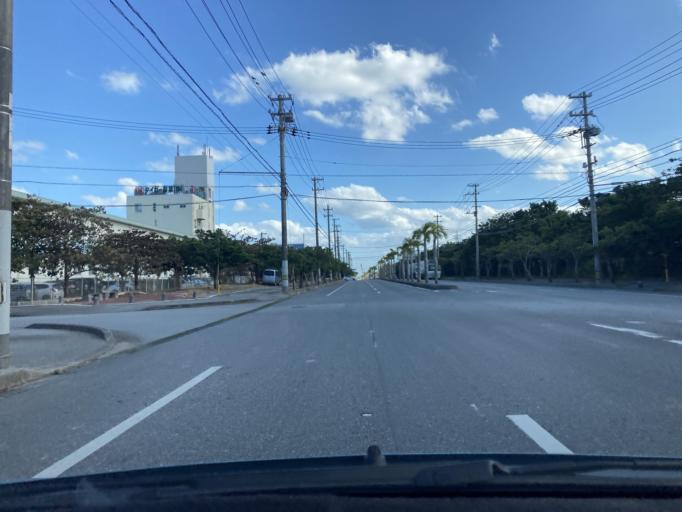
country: JP
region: Okinawa
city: Katsuren-haebaru
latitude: 26.3343
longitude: 127.8508
